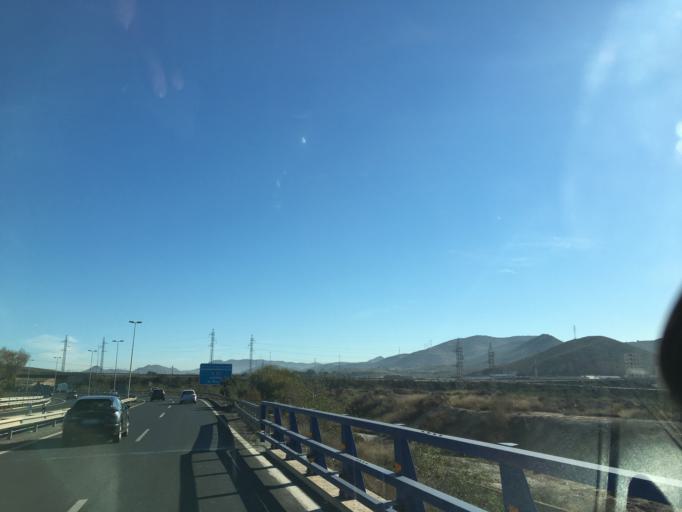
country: ES
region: Murcia
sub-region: Murcia
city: Cartagena
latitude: 37.6091
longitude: -0.9652
